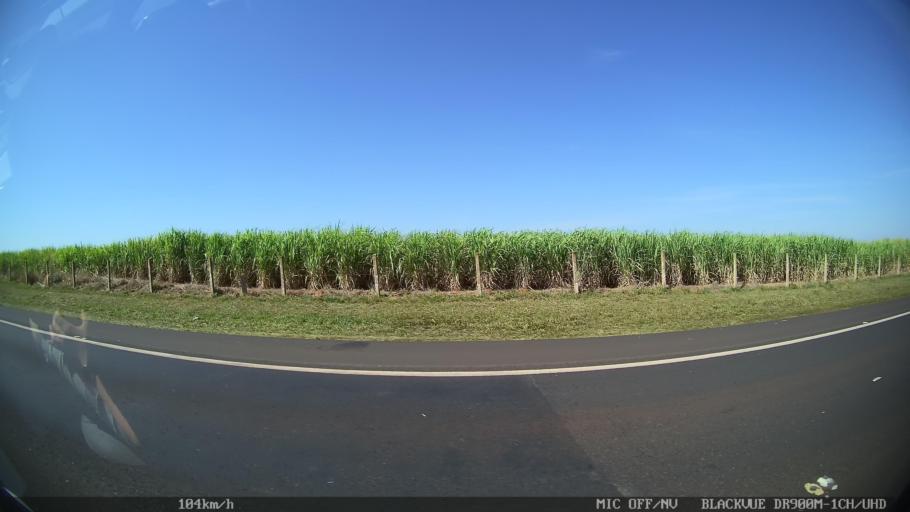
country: BR
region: Sao Paulo
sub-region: Batatais
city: Batatais
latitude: -20.8188
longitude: -47.5871
